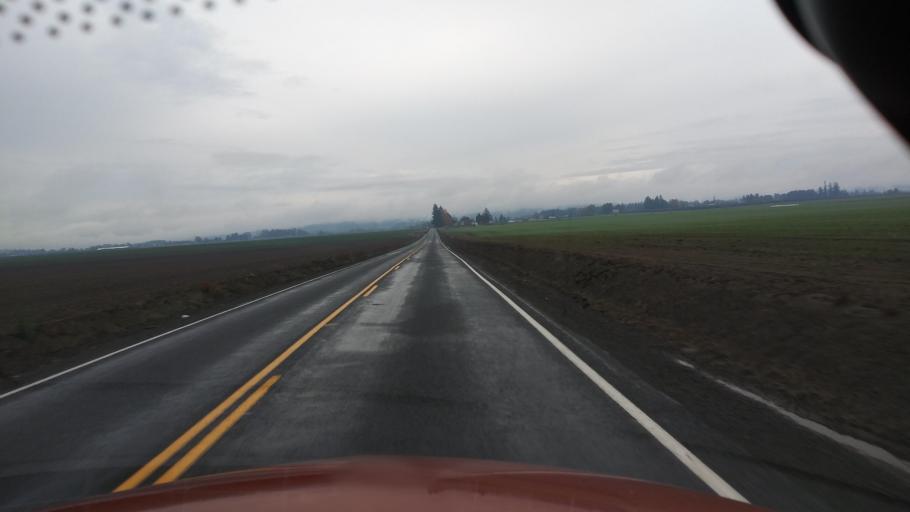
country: US
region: Oregon
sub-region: Washington County
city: North Plains
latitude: 45.5758
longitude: -123.0211
